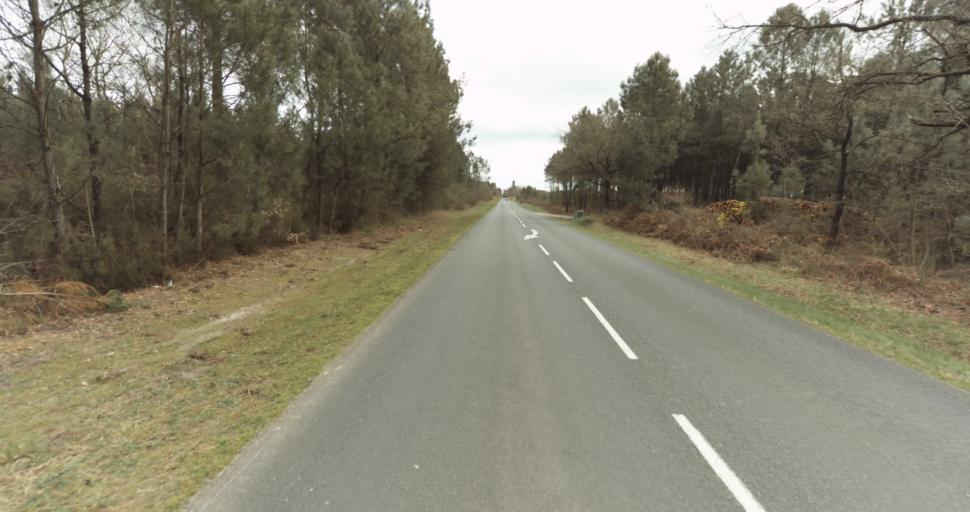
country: FR
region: Aquitaine
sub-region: Departement des Landes
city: Roquefort
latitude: 44.0604
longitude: -0.3977
